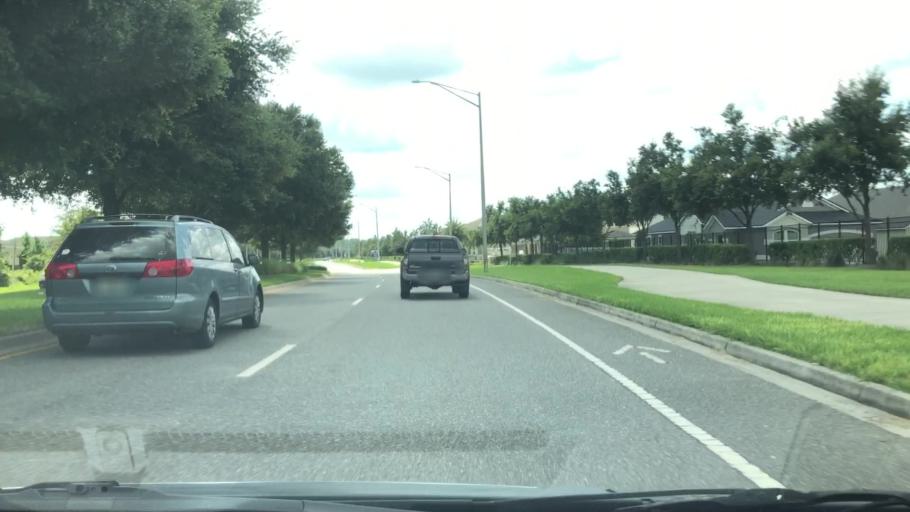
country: US
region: Florida
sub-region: Saint Johns County
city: Fruit Cove
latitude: 30.1169
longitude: -81.5216
